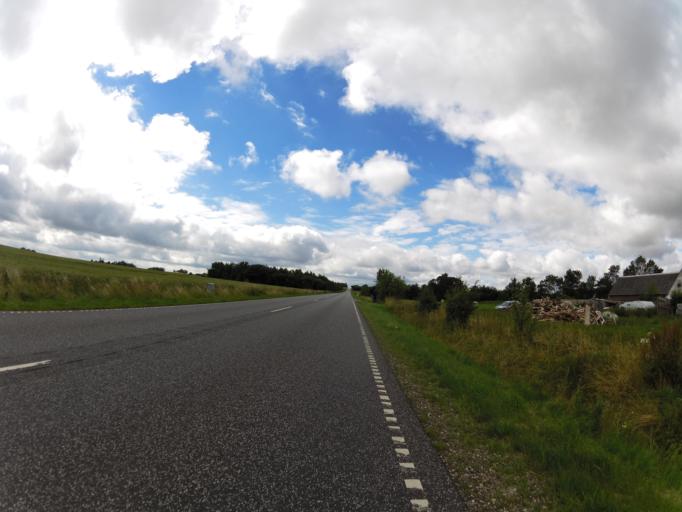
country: DK
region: North Denmark
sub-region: Mariagerfjord Kommune
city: Hadsund
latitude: 56.6052
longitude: 10.1459
